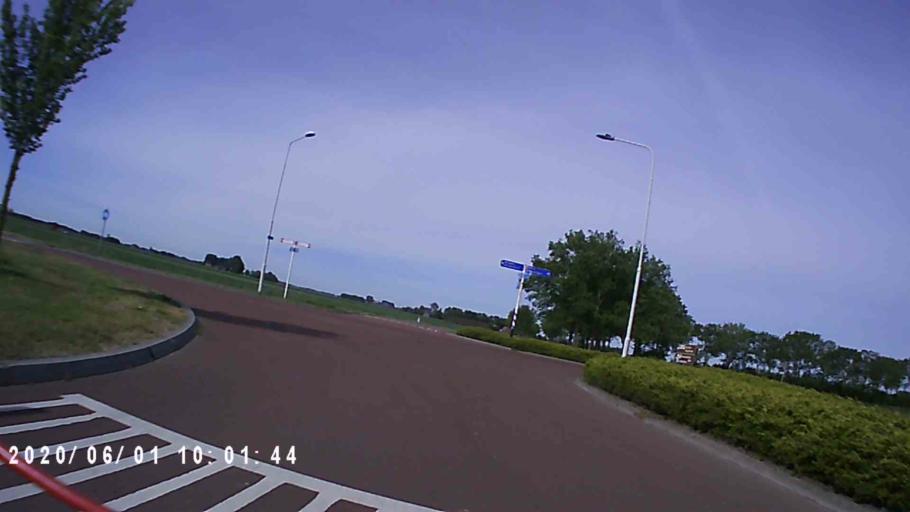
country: NL
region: Friesland
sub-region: Menameradiel
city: Berltsum
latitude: 53.2404
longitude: 5.6364
